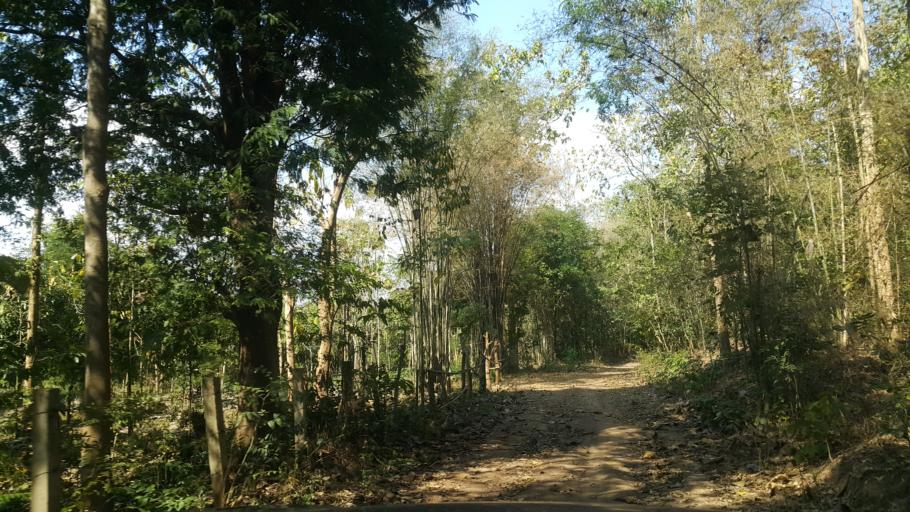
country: TH
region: Sukhothai
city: Thung Saliam
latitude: 17.3550
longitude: 99.5786
